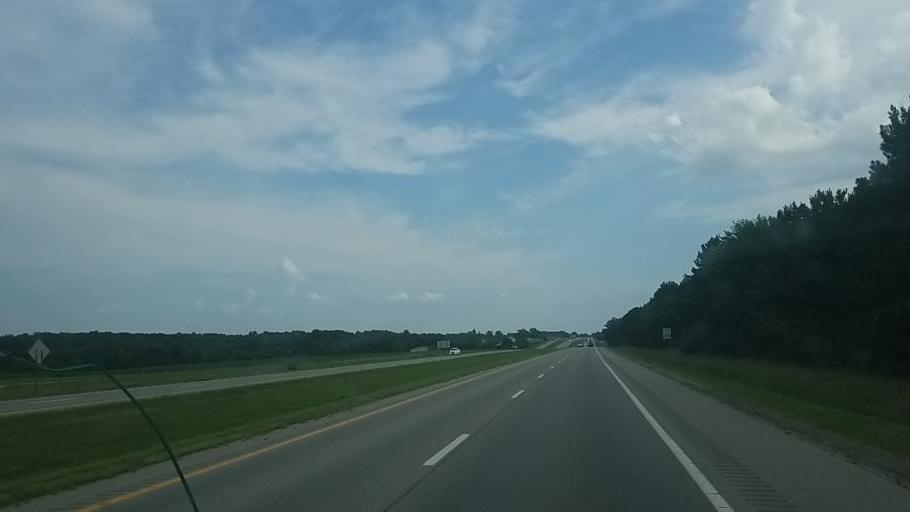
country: US
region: Ohio
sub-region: Wyandot County
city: Upper Sandusky
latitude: 40.7726
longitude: -83.2407
